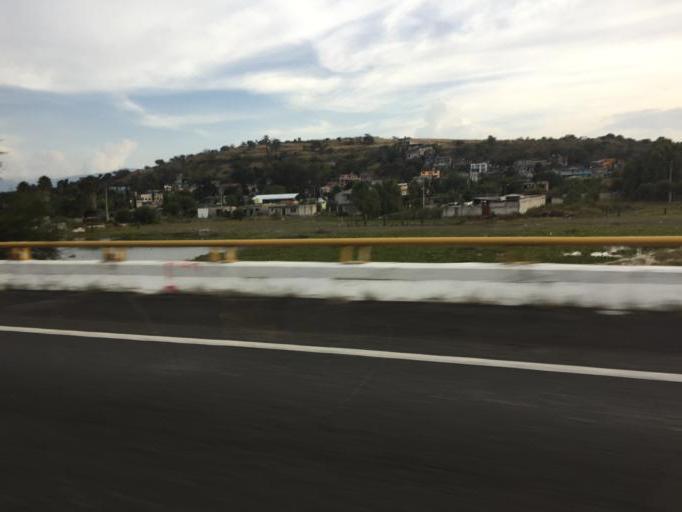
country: MX
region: Michoacan
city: Querendaro
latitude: 19.8849
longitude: -100.9464
